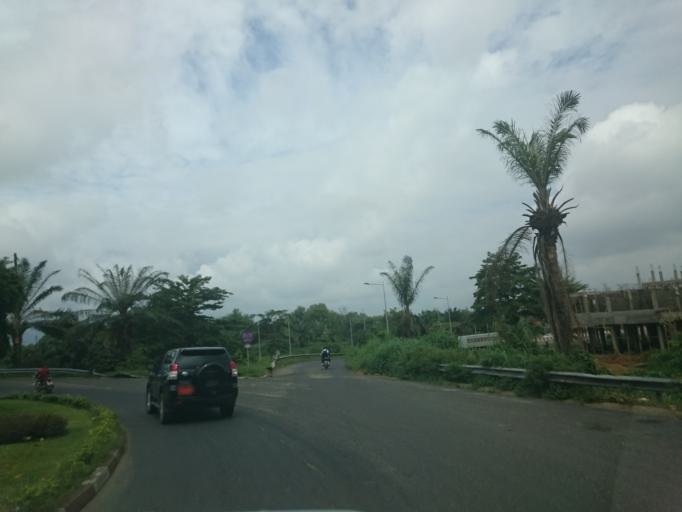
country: CM
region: Littoral
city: Douala
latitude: 4.0181
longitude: 9.6995
